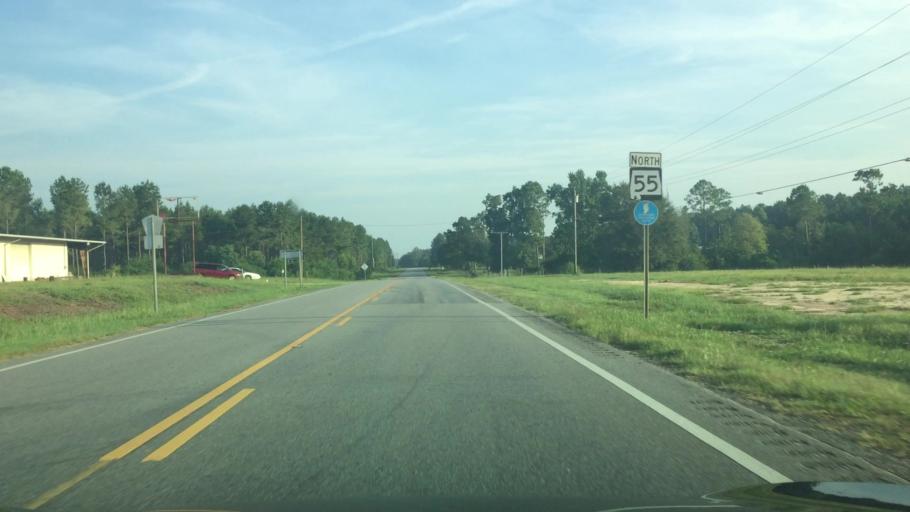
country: US
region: Alabama
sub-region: Covington County
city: Florala
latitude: 31.0166
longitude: -86.3611
